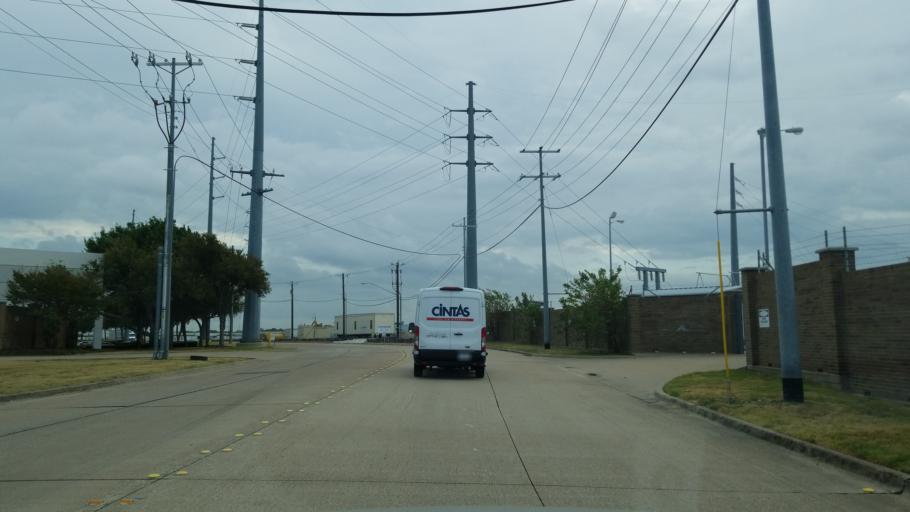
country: US
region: Texas
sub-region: Dallas County
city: Garland
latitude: 32.9015
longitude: -96.6778
